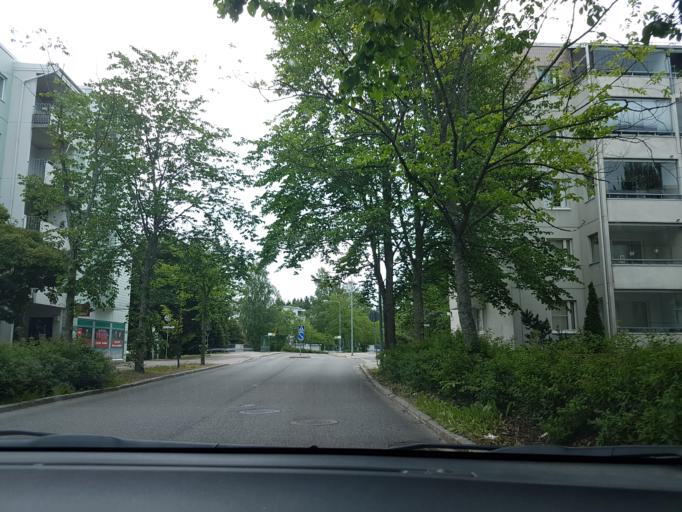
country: FI
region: Uusimaa
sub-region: Helsinki
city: Vantaa
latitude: 60.2388
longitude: 25.0946
